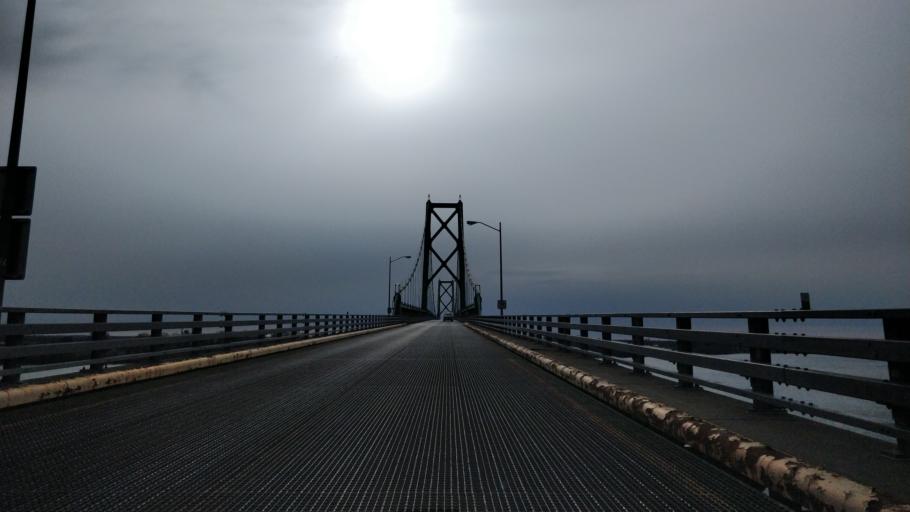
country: US
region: New York
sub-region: St. Lawrence County
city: Ogdensburg
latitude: 44.7387
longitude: -75.4621
